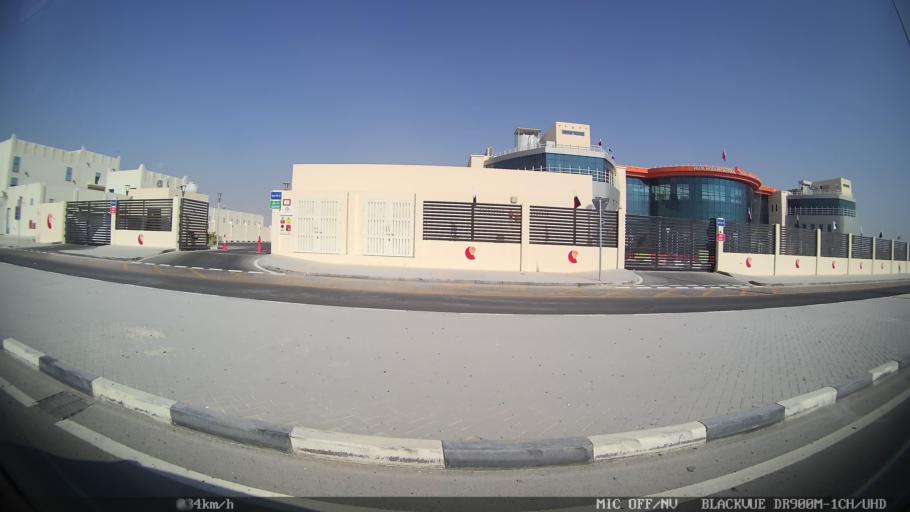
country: QA
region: Al Wakrah
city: Al Wukayr
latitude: 25.1868
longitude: 51.5623
